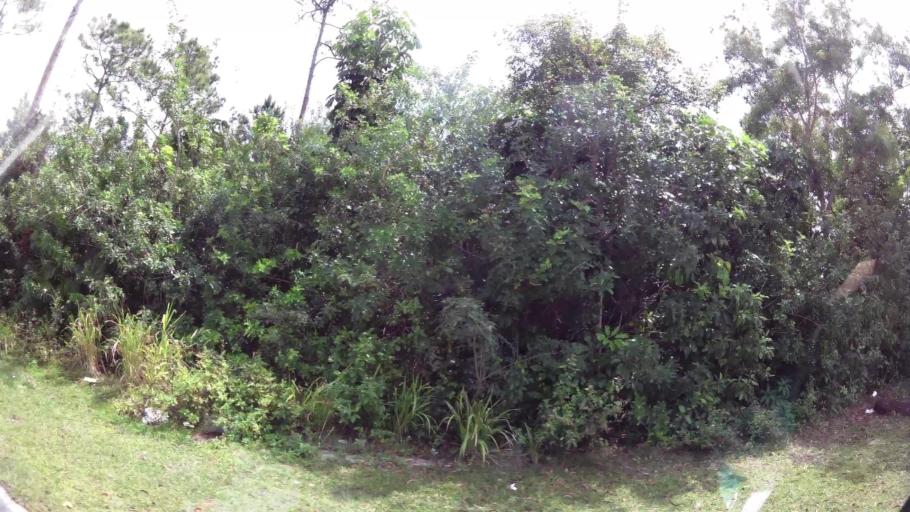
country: BS
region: Freeport
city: Lucaya
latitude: 26.5220
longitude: -78.6503
